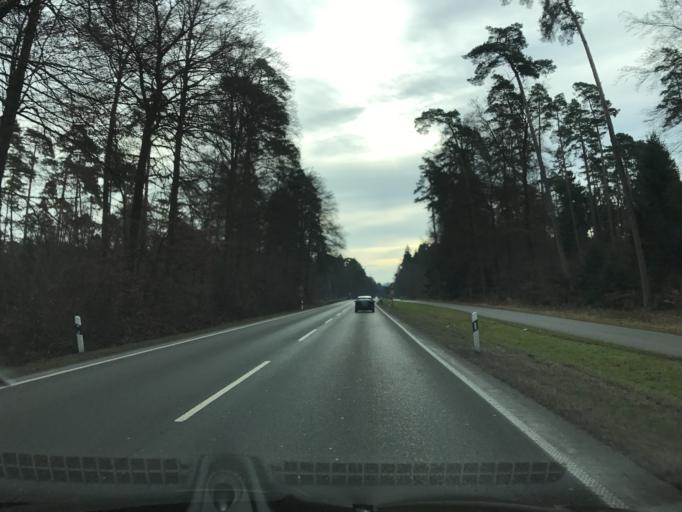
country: DE
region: Baden-Wuerttemberg
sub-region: Tuebingen Region
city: Eriskirch
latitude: 47.6250
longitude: 9.5517
